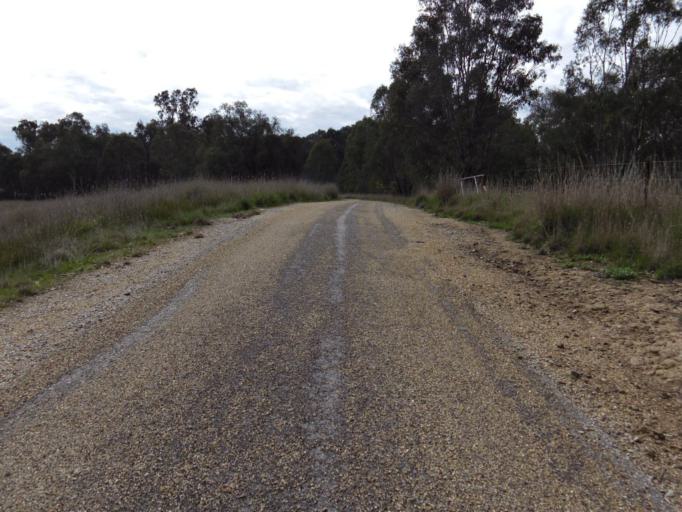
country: AU
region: Victoria
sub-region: Wangaratta
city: Wangaratta
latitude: -36.3928
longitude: 146.3439
